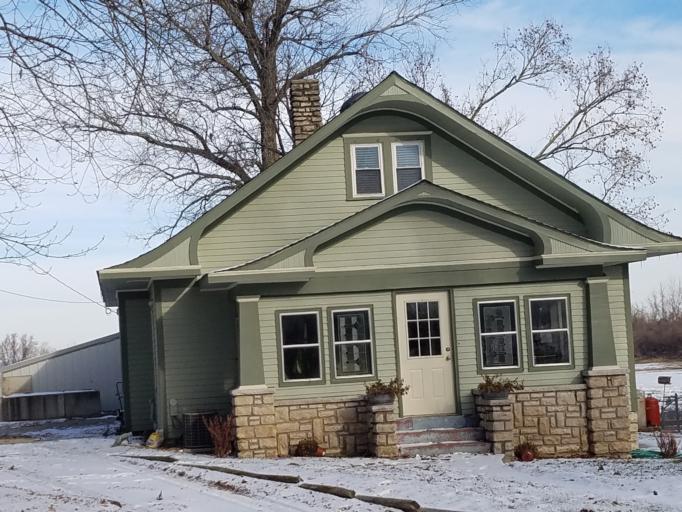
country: US
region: Missouri
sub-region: Ray County
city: Albany
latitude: 39.1318
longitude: -94.0700
